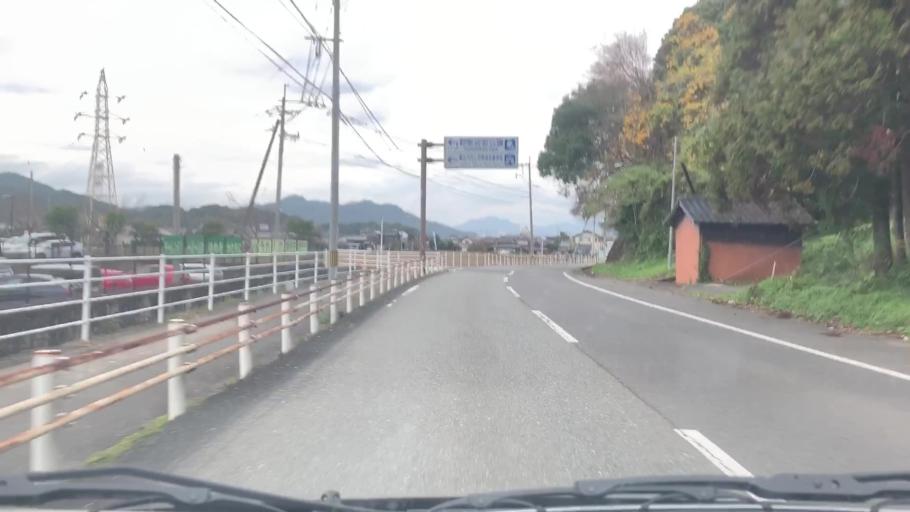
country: JP
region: Saga Prefecture
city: Kashima
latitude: 33.1191
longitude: 130.0636
